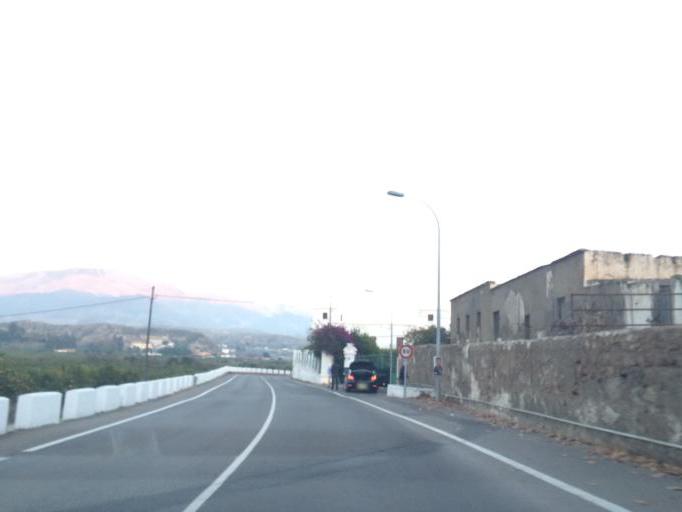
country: ES
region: Andalusia
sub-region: Provincia de Almeria
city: Gador
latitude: 36.9511
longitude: -2.4848
